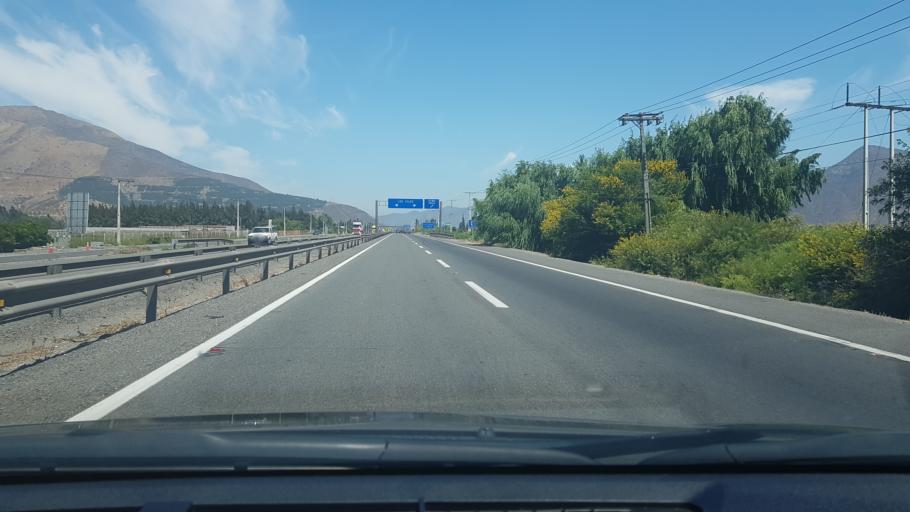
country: CL
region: Valparaiso
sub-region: Provincia de San Felipe
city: Llaillay
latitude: -32.8466
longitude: -70.9708
